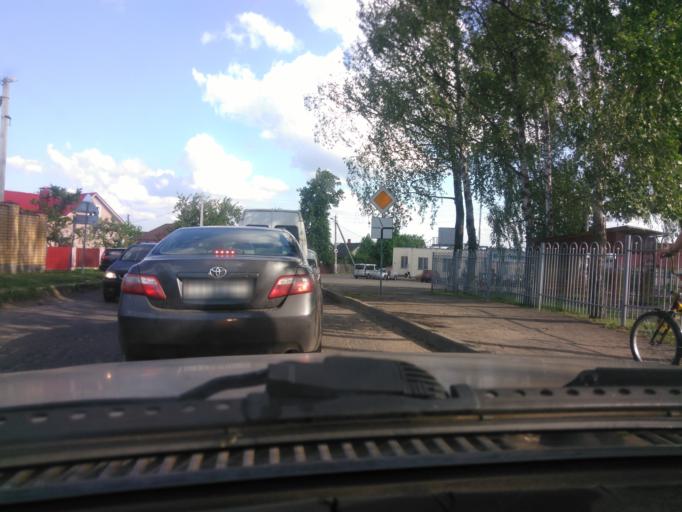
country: BY
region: Mogilev
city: Mahilyow
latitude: 53.9288
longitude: 30.3182
